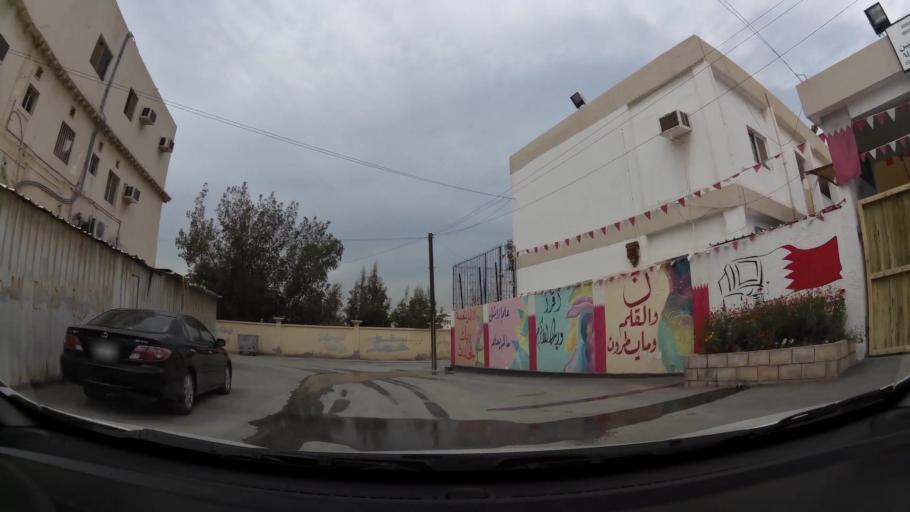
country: BH
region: Manama
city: Manama
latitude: 26.1853
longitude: 50.5825
